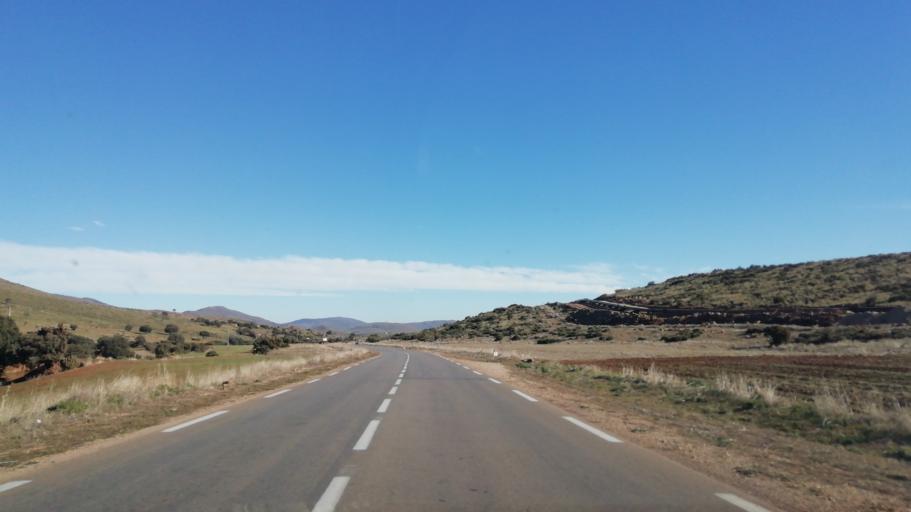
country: DZ
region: Tlemcen
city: Ouled Mimoun
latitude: 34.7508
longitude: -1.1570
